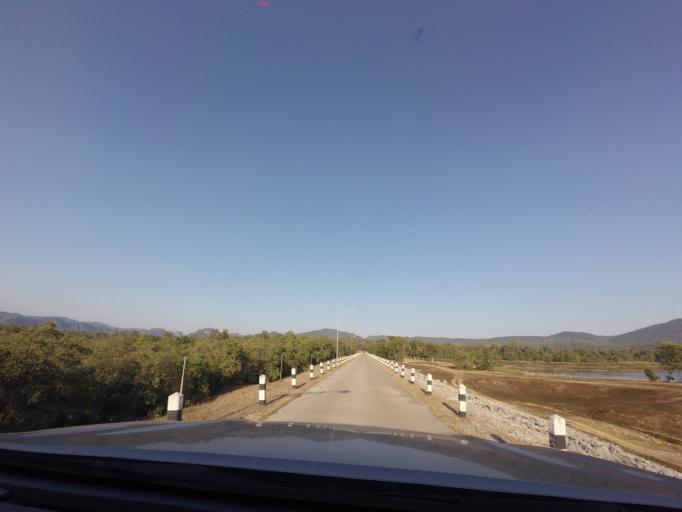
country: TH
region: Lampang
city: Mae Mo
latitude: 18.3860
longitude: 99.7574
